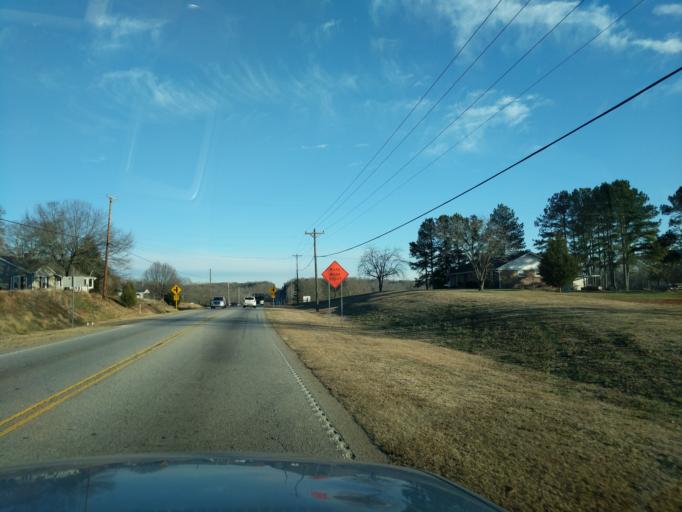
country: US
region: South Carolina
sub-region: Anderson County
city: Williamston
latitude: 34.6397
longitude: -82.4315
